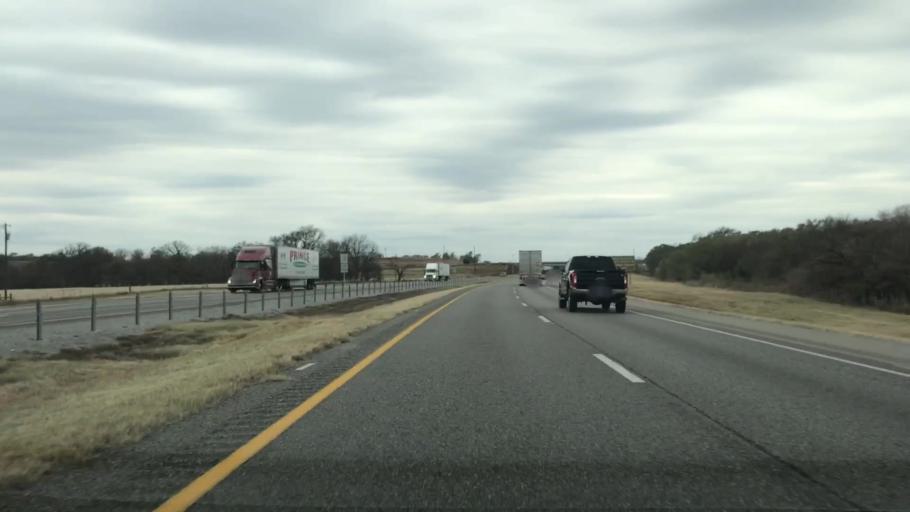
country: US
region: Oklahoma
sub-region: Custer County
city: Clinton
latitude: 35.5002
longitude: -98.9530
